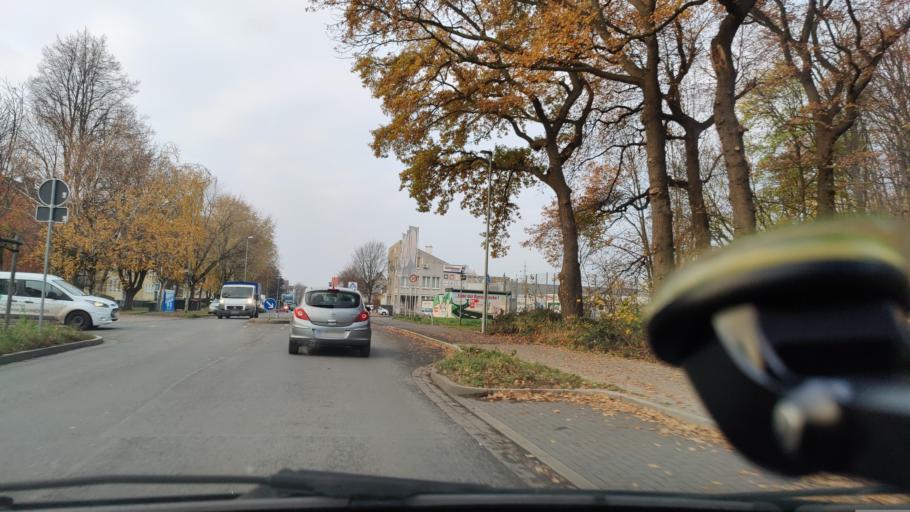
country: DE
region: North Rhine-Westphalia
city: Lunen
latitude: 51.5906
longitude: 7.5370
